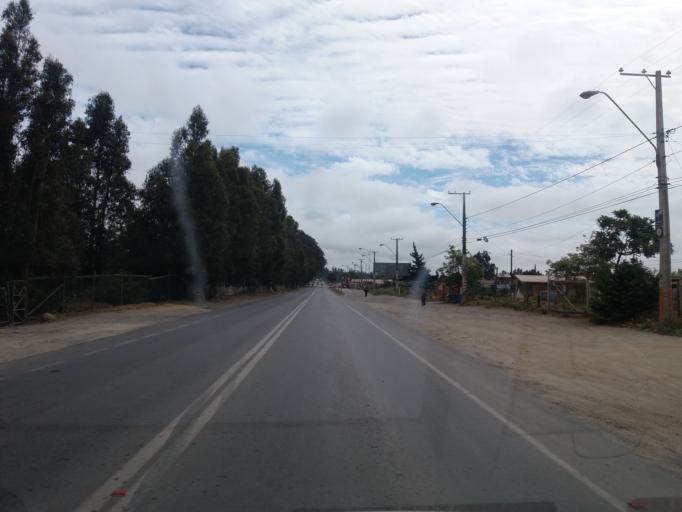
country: CL
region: Valparaiso
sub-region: Provincia de Marga Marga
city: Quilpue
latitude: -32.9293
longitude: -71.4293
